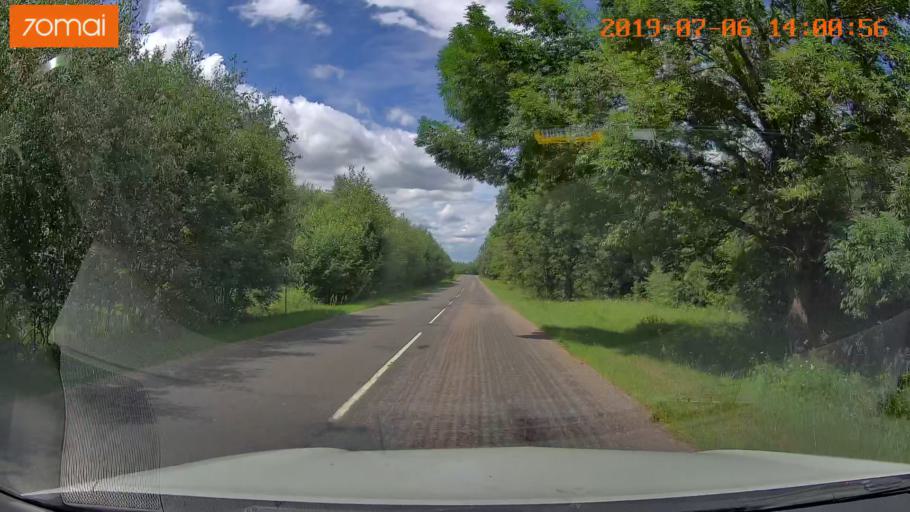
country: BY
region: Minsk
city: Ivyanyets
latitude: 53.8032
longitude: 26.8179
